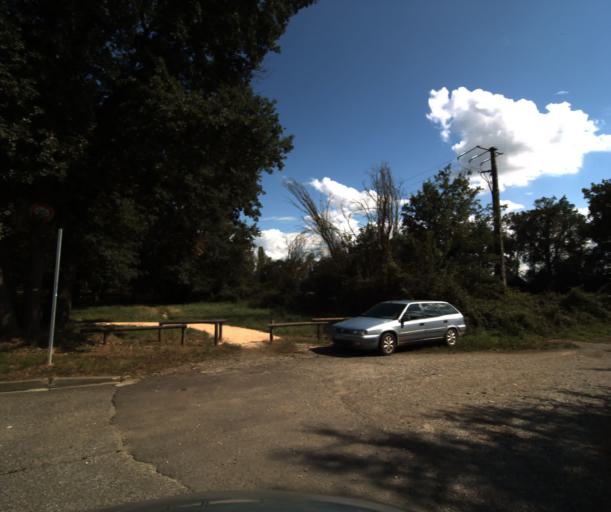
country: FR
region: Midi-Pyrenees
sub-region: Departement de la Haute-Garonne
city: Roquettes
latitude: 43.4926
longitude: 1.3636
